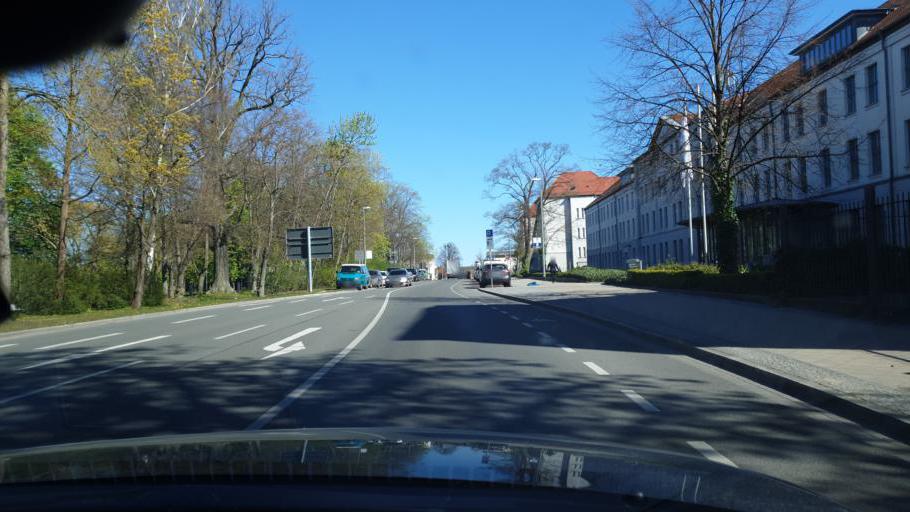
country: DE
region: Mecklenburg-Vorpommern
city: Werdervorstadt
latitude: 53.6379
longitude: 11.4236
